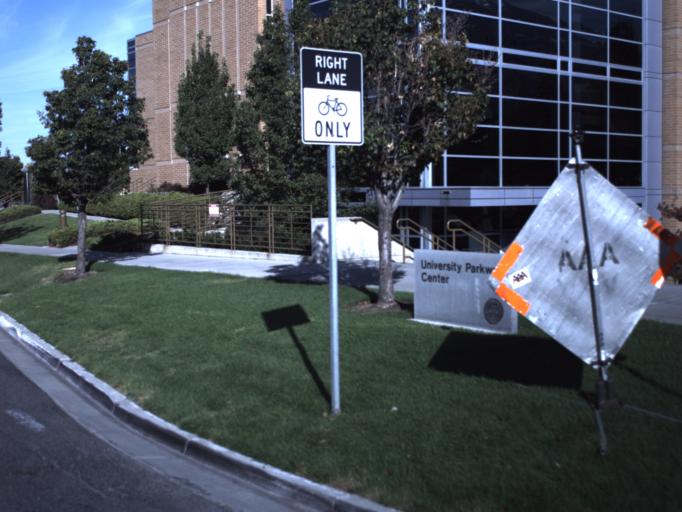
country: US
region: Utah
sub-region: Utah County
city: Provo
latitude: 40.2559
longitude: -111.6576
